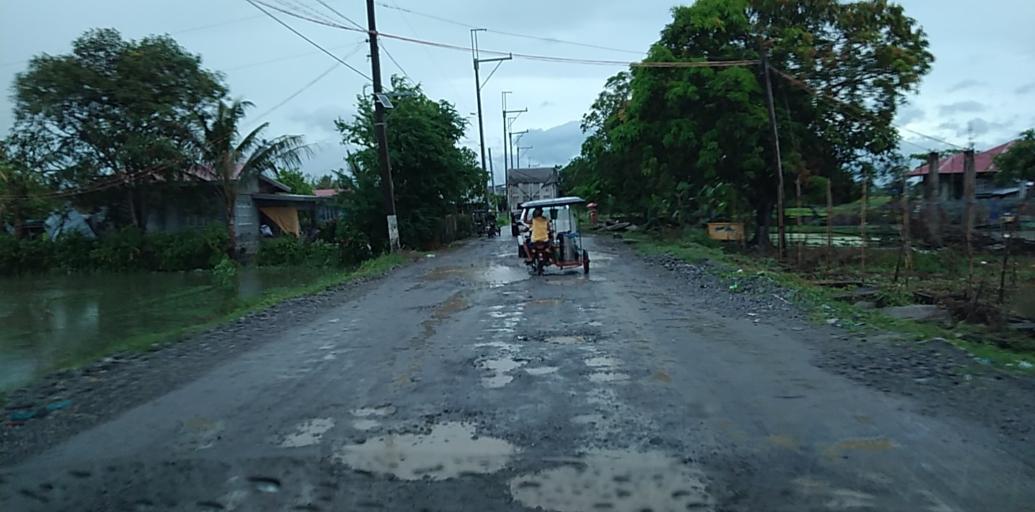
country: PH
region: Central Luzon
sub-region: Province of Pampanga
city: Salapungan
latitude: 15.1348
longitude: 120.9201
